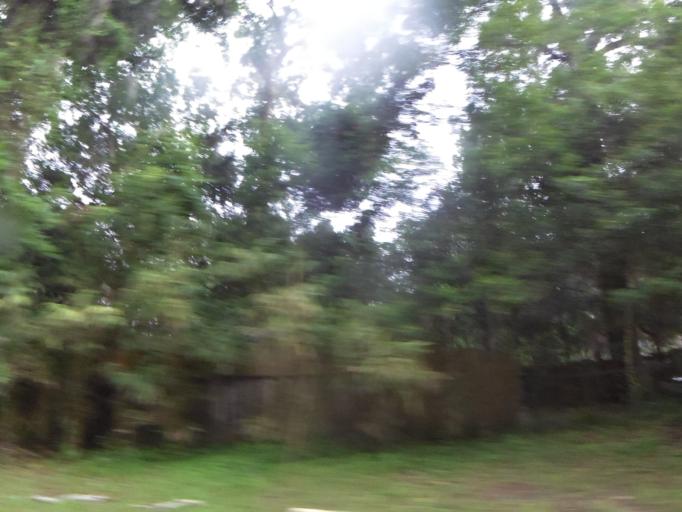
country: US
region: Florida
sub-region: Duval County
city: Jacksonville
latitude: 30.3430
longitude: -81.6063
